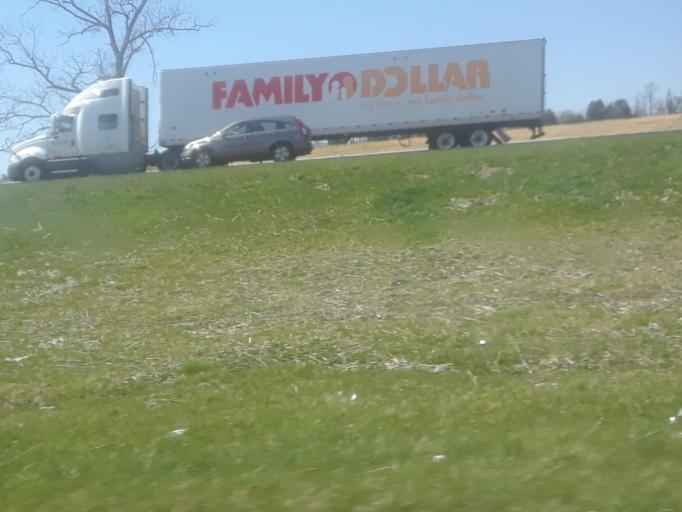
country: US
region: Virginia
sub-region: Shenandoah County
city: New Market
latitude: 38.6712
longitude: -78.6630
